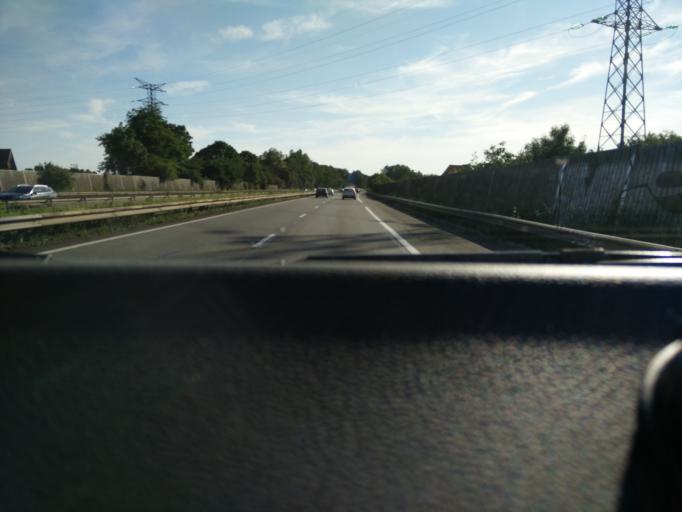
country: FR
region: Nord-Pas-de-Calais
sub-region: Departement du Nord
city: Haulchin
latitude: 50.3196
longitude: 3.4213
